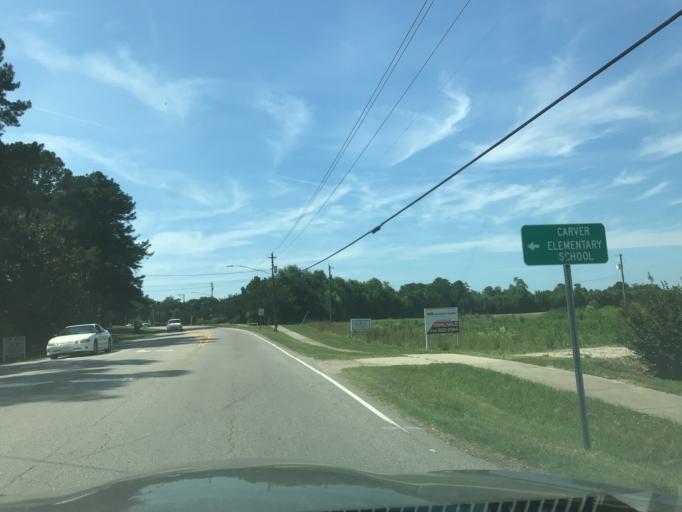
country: US
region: North Carolina
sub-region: Wake County
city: Wendell
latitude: 35.7927
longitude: -78.3789
